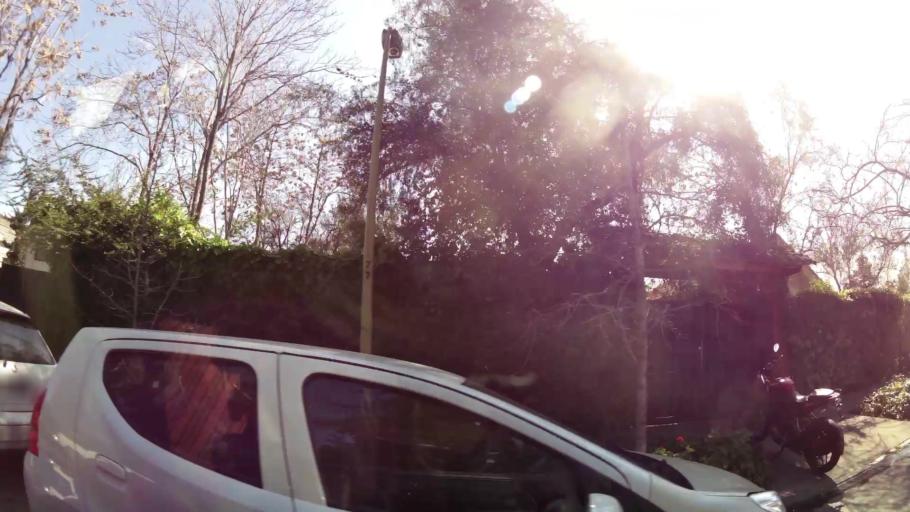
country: CL
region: Santiago Metropolitan
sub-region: Provincia de Santiago
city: Villa Presidente Frei, Nunoa, Santiago, Chile
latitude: -33.4003
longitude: -70.5412
